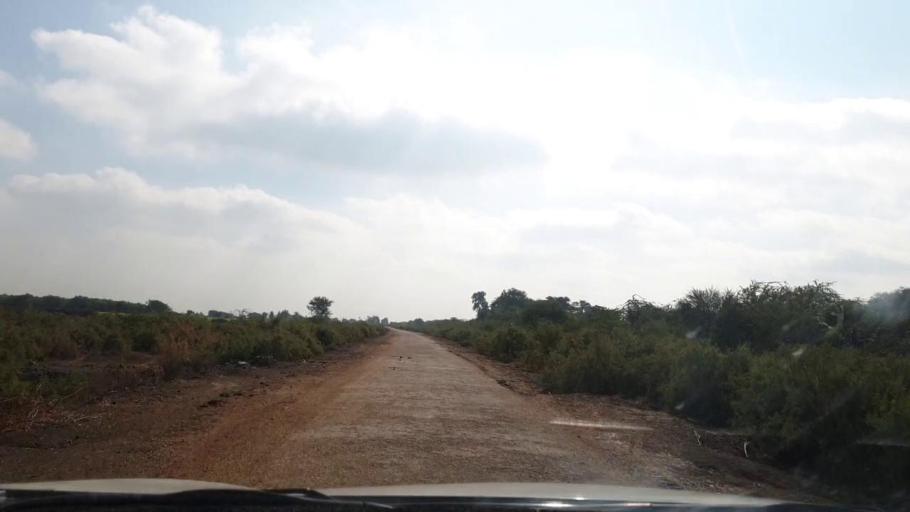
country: PK
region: Sindh
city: Berani
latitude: 25.7842
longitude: 68.9648
